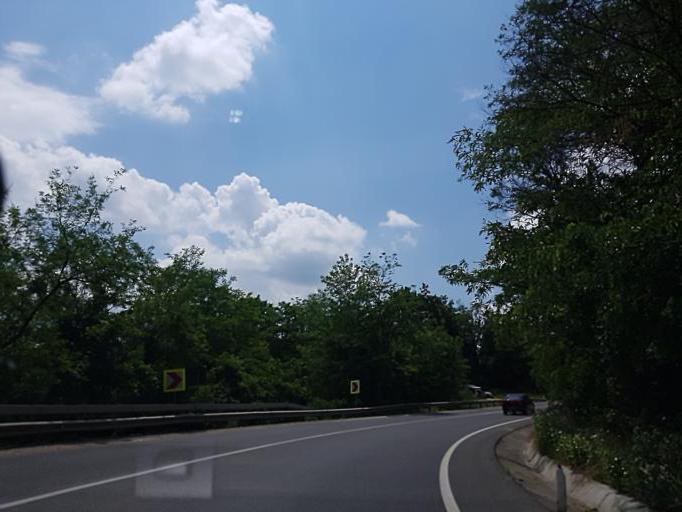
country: RO
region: Sibiu
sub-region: Comuna Slimnic
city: Slimnic
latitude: 45.9482
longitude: 24.1772
